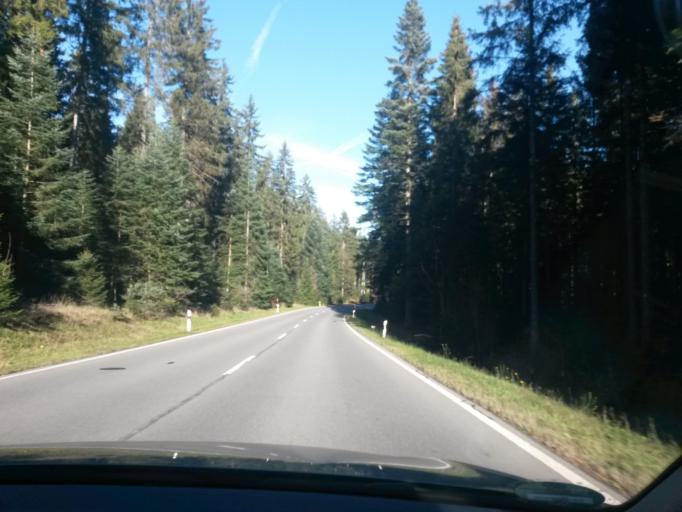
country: DE
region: Baden-Wuerttemberg
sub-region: Karlsruhe Region
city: Simmersfeld
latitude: 48.6408
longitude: 8.5053
